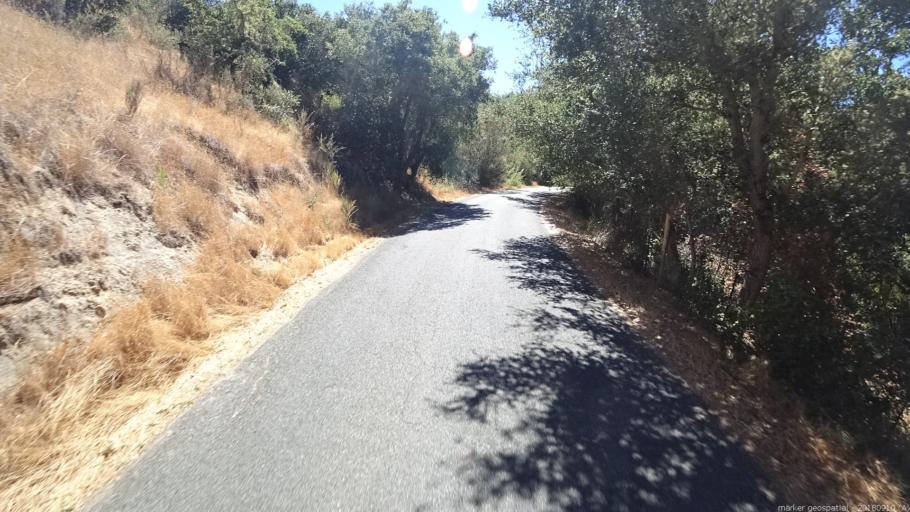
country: US
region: California
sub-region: Monterey County
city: Carmel Valley Village
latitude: 36.4742
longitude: -121.8004
